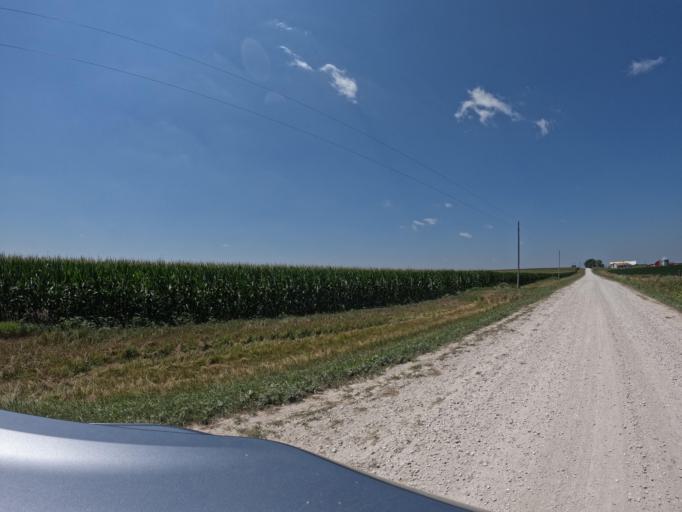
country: US
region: Iowa
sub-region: Keokuk County
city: Sigourney
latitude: 41.2886
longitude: -92.2234
